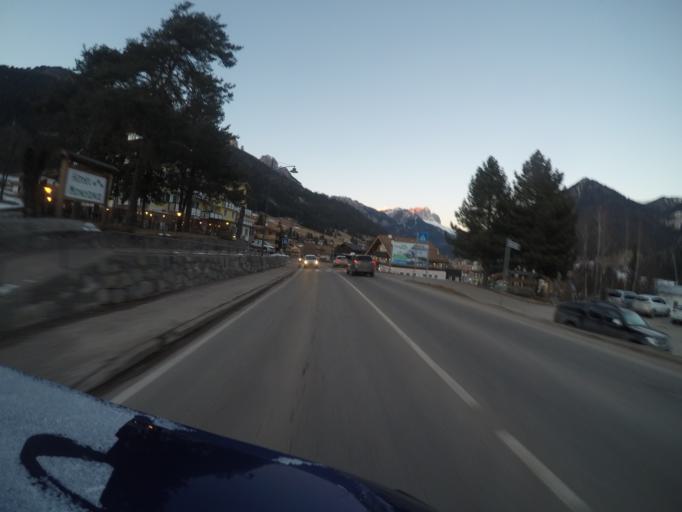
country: IT
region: Trentino-Alto Adige
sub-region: Provincia di Trento
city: Pozza di Fassa
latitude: 46.4245
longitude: 11.6828
